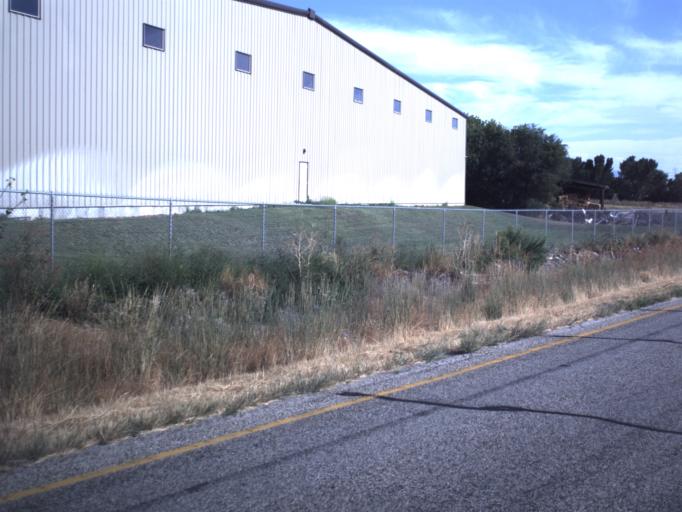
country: US
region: Utah
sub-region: Box Elder County
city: South Willard
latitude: 41.3490
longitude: -112.0366
